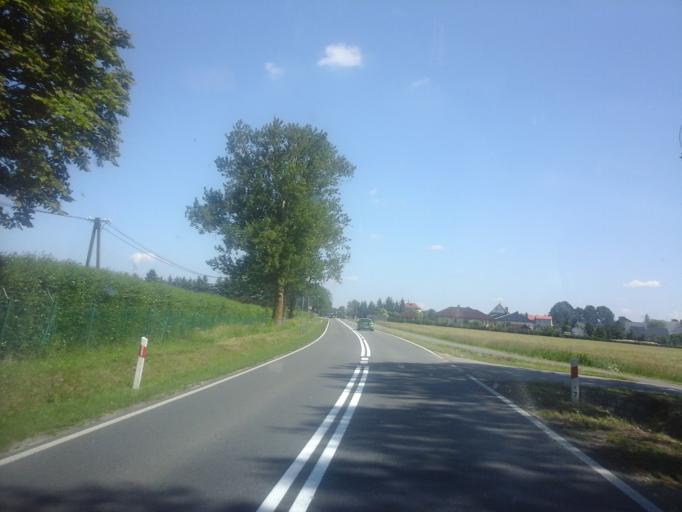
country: PL
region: West Pomeranian Voivodeship
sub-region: Koszalin
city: Koszalin
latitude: 54.1431
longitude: 16.1720
